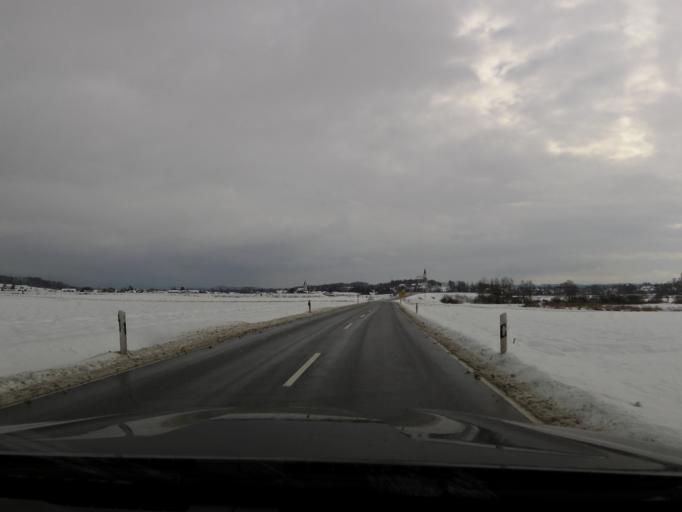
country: DE
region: Bavaria
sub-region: Lower Bavaria
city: Hengersberg
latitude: 48.7845
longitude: 13.0377
